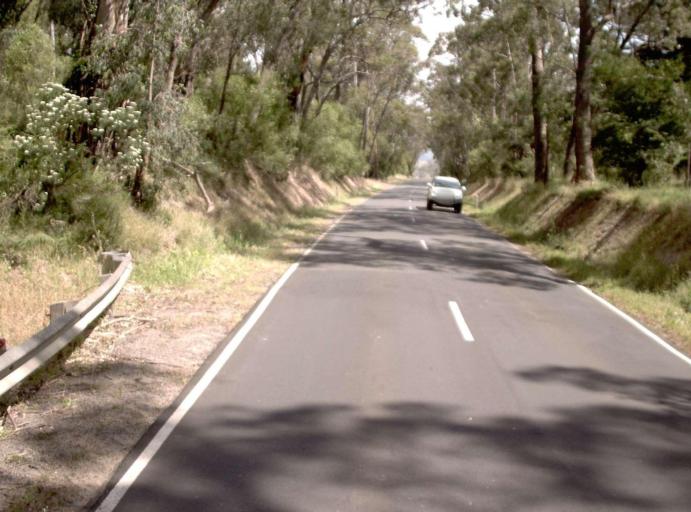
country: AU
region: Victoria
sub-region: Latrobe
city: Traralgon
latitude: -38.2919
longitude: 146.5393
